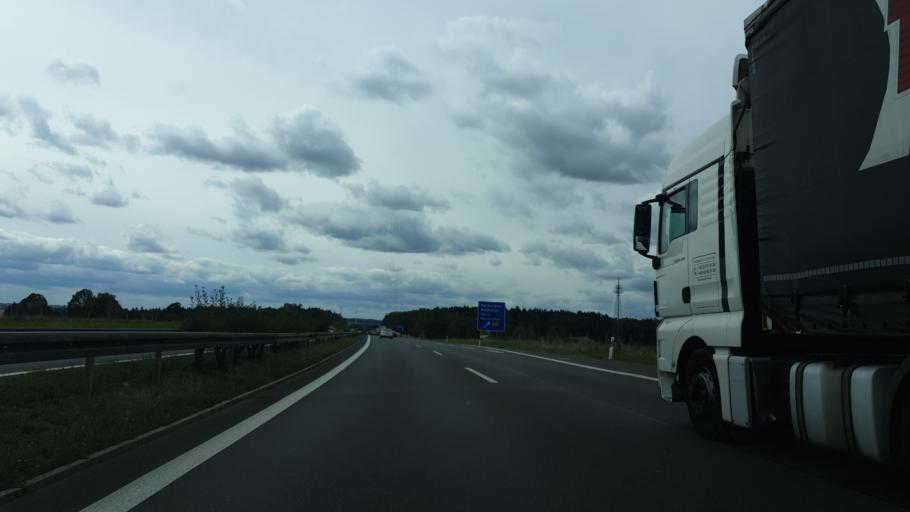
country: DE
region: Saxony
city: Lengenfeld
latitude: 50.5971
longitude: 12.3417
